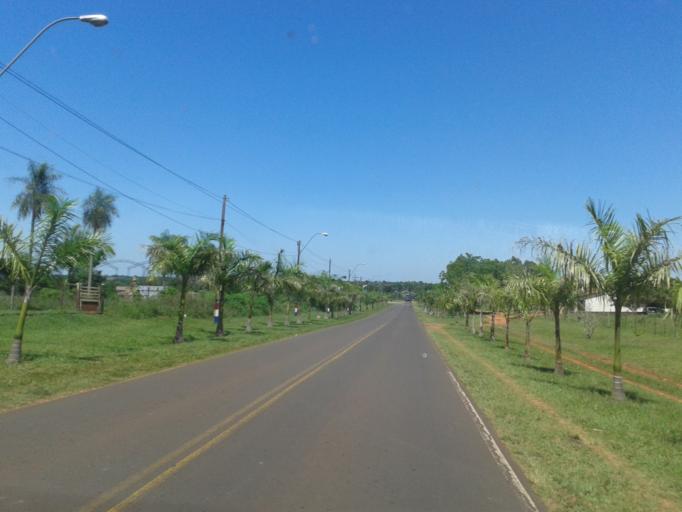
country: PY
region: Misiones
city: Santa Rosa
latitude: -26.8890
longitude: -56.8644
